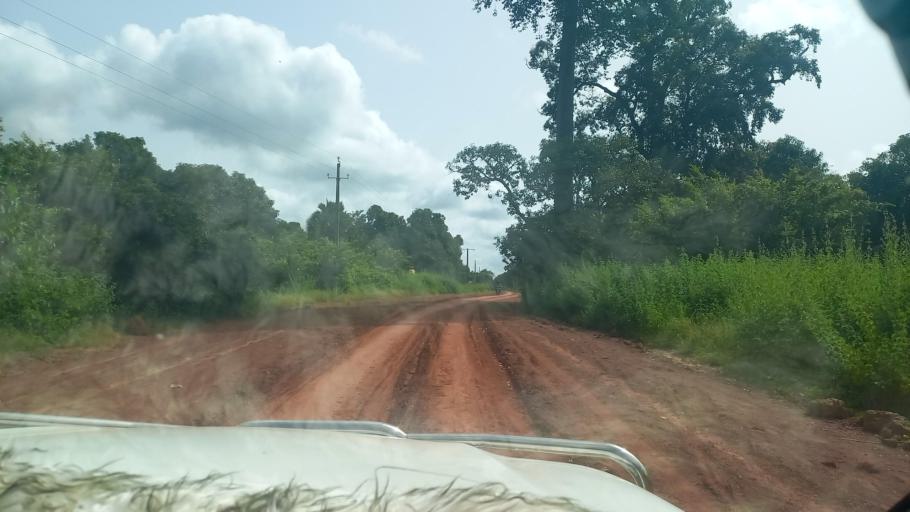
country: SN
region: Ziguinchor
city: Bignona
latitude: 12.7559
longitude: -16.2705
